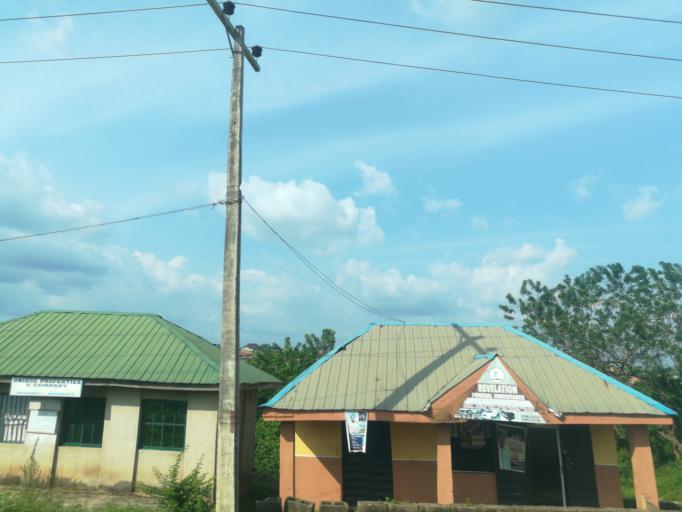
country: NG
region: Oyo
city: Ido
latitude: 7.3991
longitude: 3.8048
